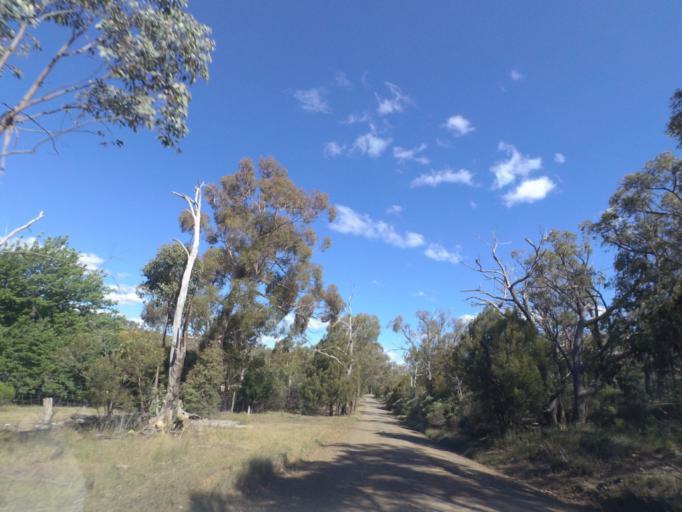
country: AU
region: Victoria
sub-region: Hume
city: Sunbury
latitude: -37.4368
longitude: 144.6635
